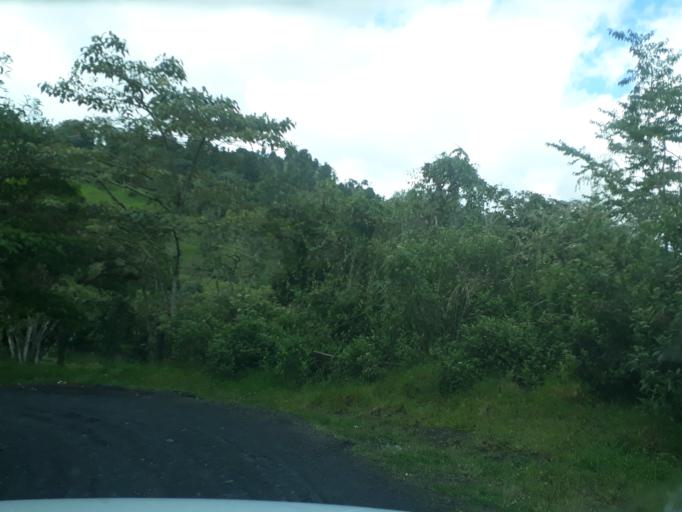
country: CO
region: Cundinamarca
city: Carmen de Carupa
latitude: 5.3439
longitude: -74.0546
